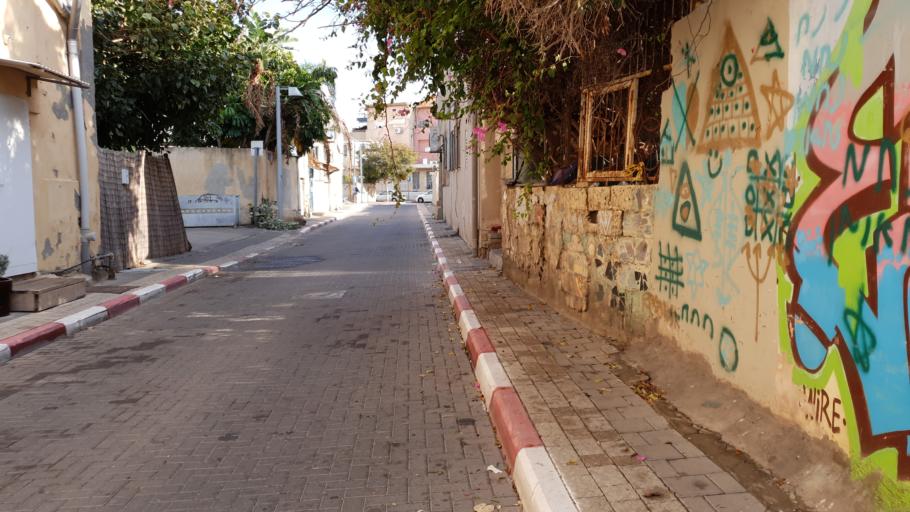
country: IL
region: Tel Aviv
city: Yafo
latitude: 32.0641
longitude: 34.7646
